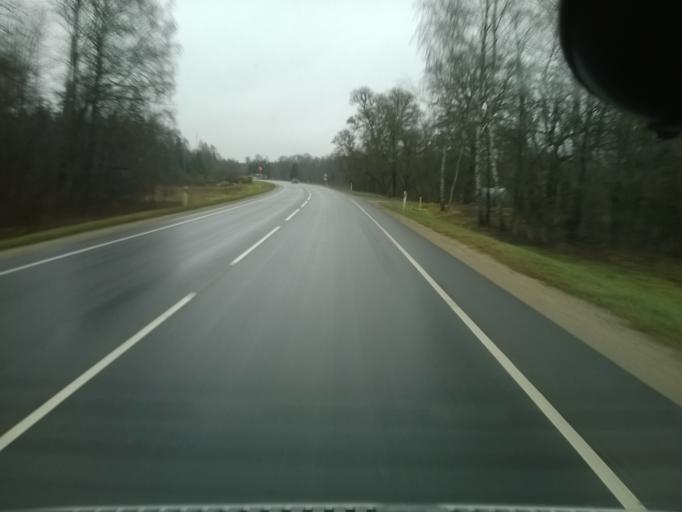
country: EE
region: Harju
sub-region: Nissi vald
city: Turba
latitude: 59.0590
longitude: 24.1915
